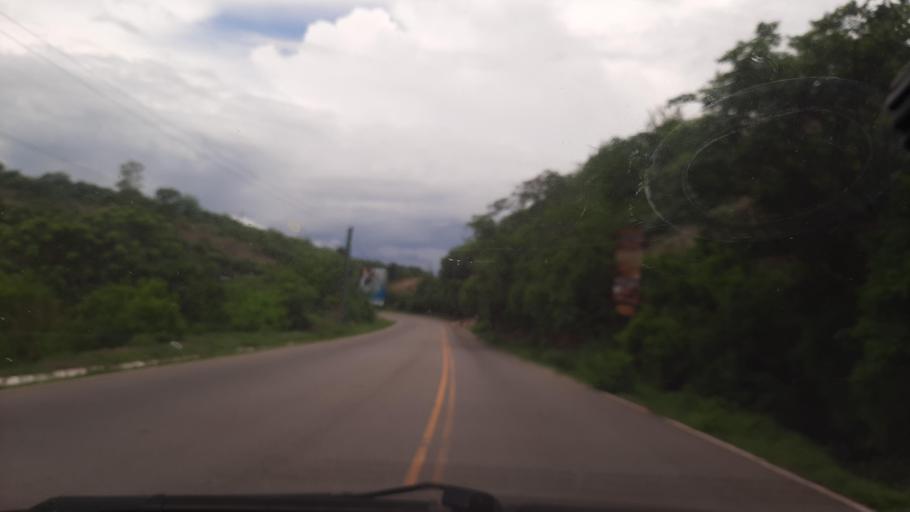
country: GT
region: Chiquimula
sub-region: Municipio de Chiquimula
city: Chiquimula
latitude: 14.8631
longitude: -89.5150
